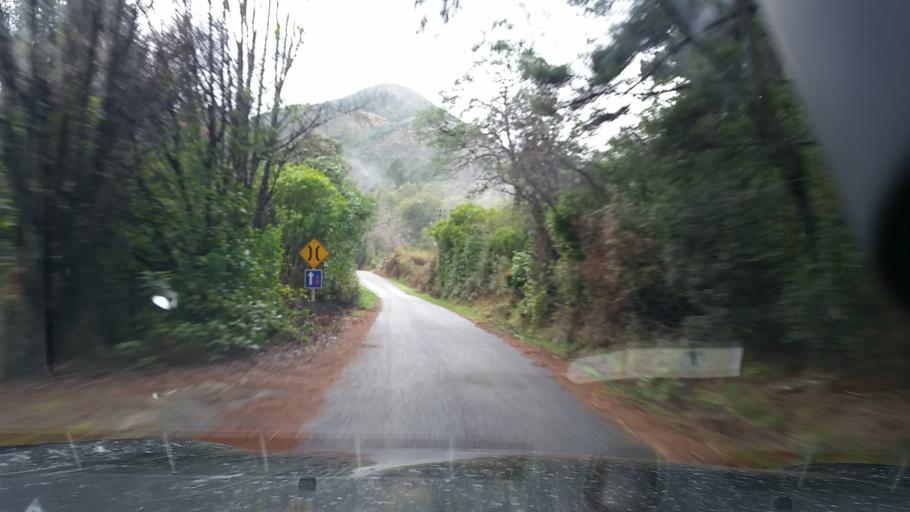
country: NZ
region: Nelson
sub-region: Nelson City
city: Nelson
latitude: -41.3557
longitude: 173.6290
